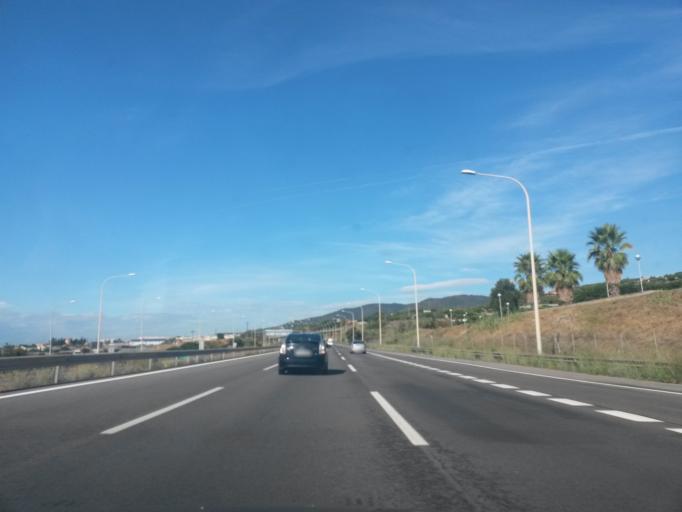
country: ES
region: Catalonia
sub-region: Provincia de Barcelona
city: Cabrera de Mar
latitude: 41.5188
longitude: 2.3966
